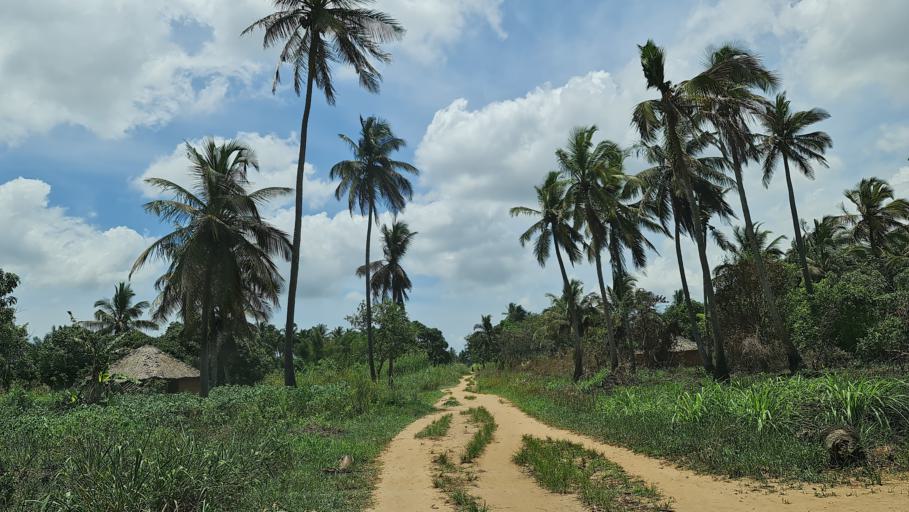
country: MZ
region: Zambezia
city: Quelimane
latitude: -17.5708
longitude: 37.3734
